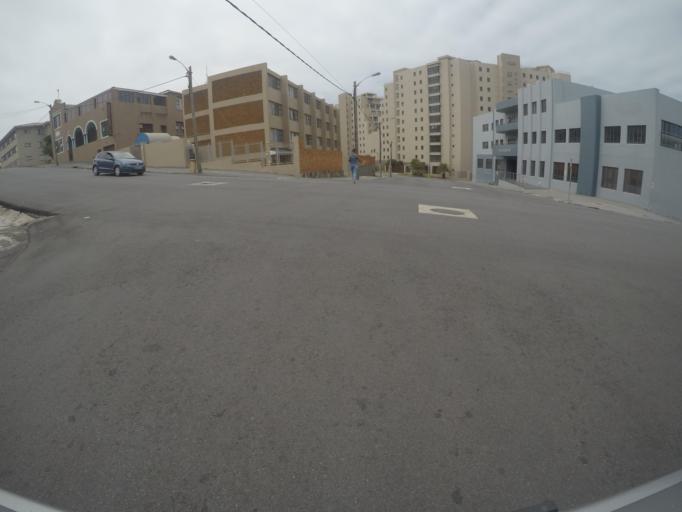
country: ZA
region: Eastern Cape
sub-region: Buffalo City Metropolitan Municipality
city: East London
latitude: -33.0186
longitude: 27.9169
